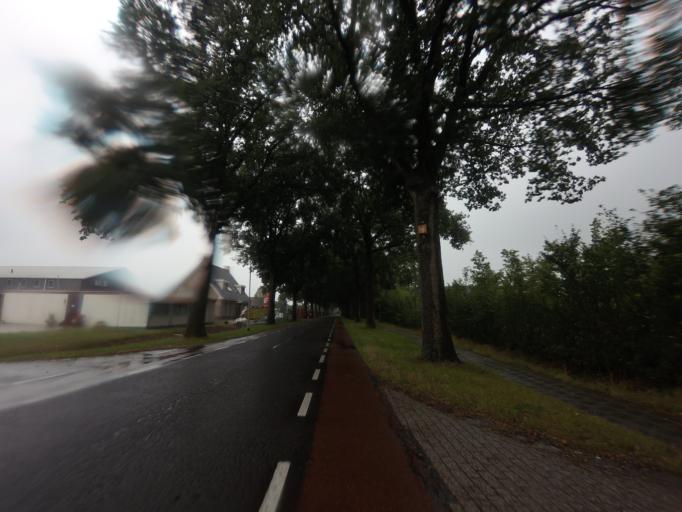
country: NL
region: Drenthe
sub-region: Gemeente Hoogeveen
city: Hoogeveen
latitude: 52.6061
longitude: 6.3943
